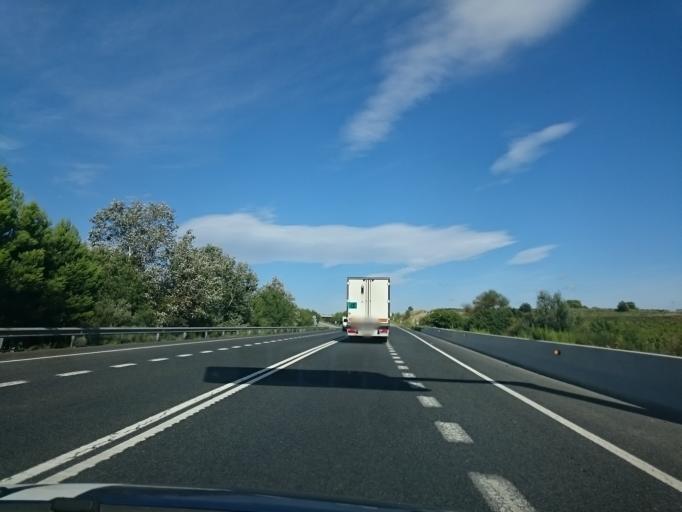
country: ES
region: Catalonia
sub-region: Provincia de Barcelona
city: Vilobi del Penedes
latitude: 41.3281
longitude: 1.6478
